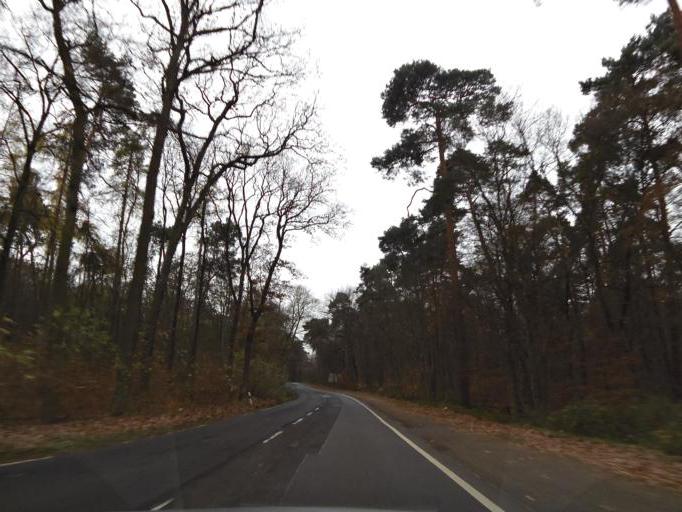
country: DE
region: Hesse
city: Kelsterbach
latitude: 50.0733
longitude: 8.5766
